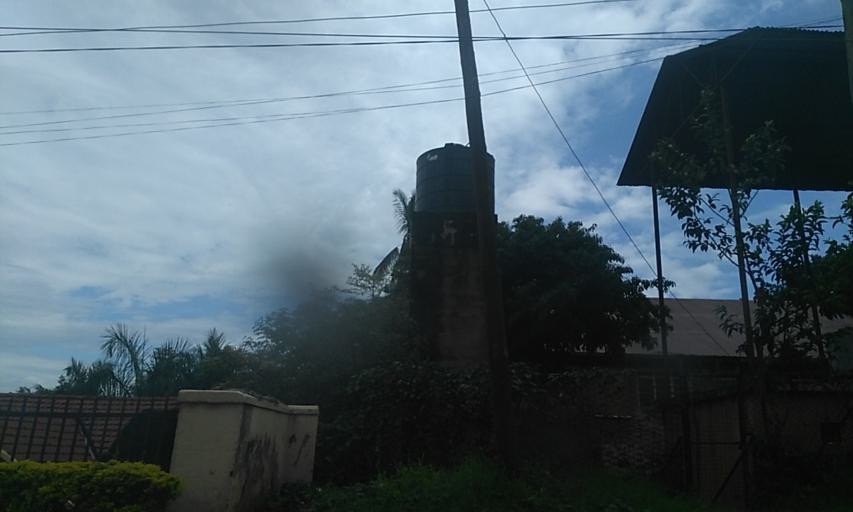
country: UG
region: Central Region
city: Kampala Central Division
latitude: 0.3392
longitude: 32.5884
